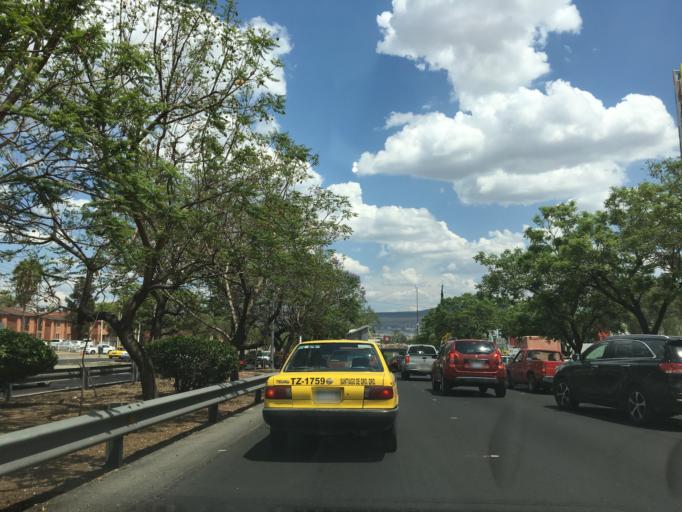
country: MX
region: Queretaro
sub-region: Queretaro
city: Santiago de Queretaro
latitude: 20.6063
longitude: -100.3779
